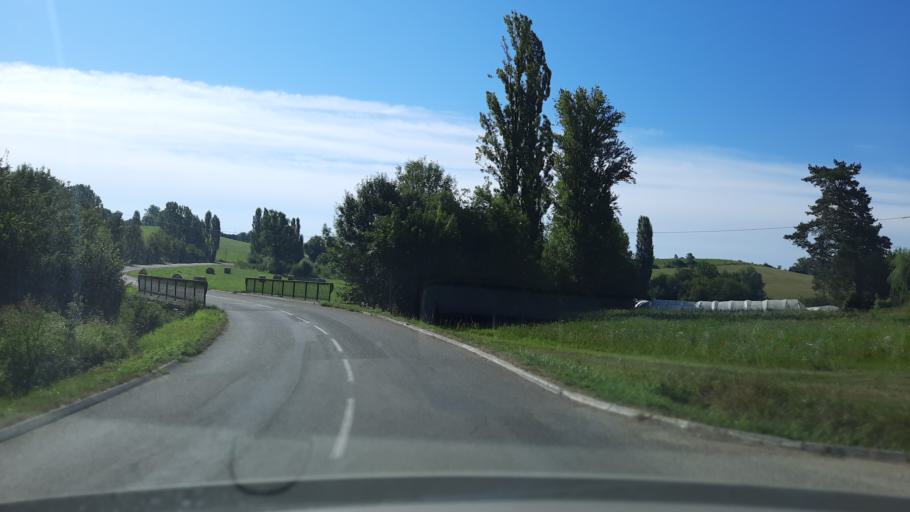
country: FR
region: Midi-Pyrenees
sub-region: Departement du Tarn-et-Garonne
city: Molieres
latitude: 44.1984
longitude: 1.4292
